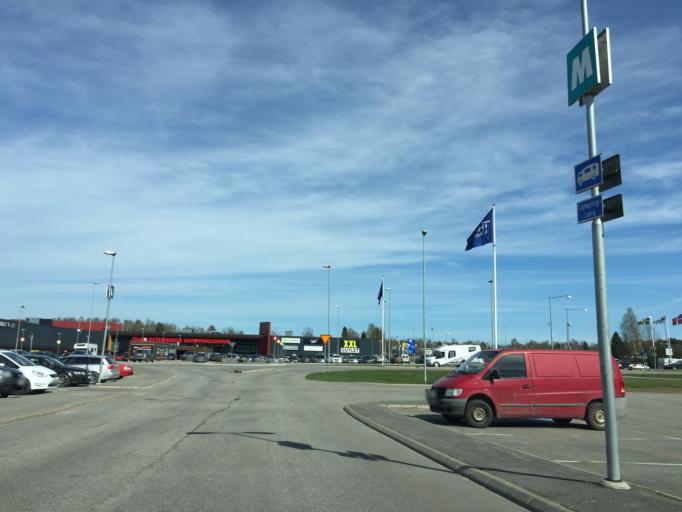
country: SE
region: Vaermland
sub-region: Eda Kommun
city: Charlottenberg
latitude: 59.8799
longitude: 12.2877
